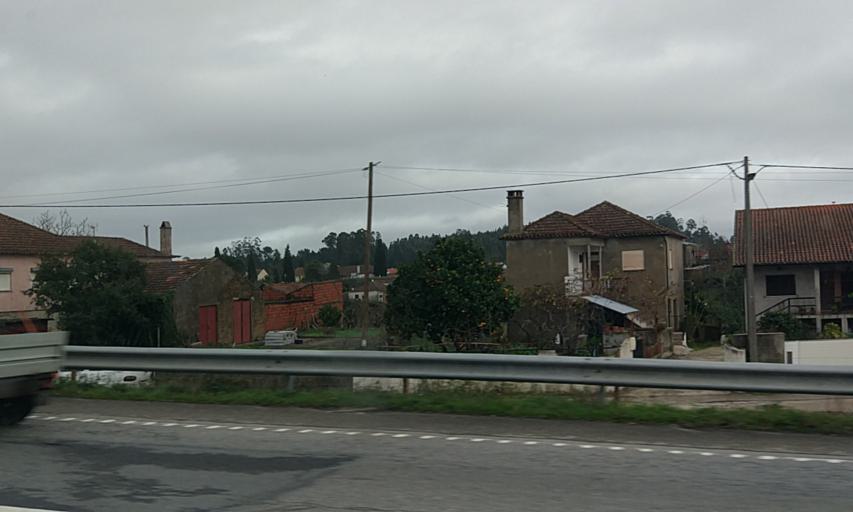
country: PT
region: Viseu
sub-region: Santa Comba Dao
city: Santa Comba Dao
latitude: 40.4172
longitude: -8.1213
